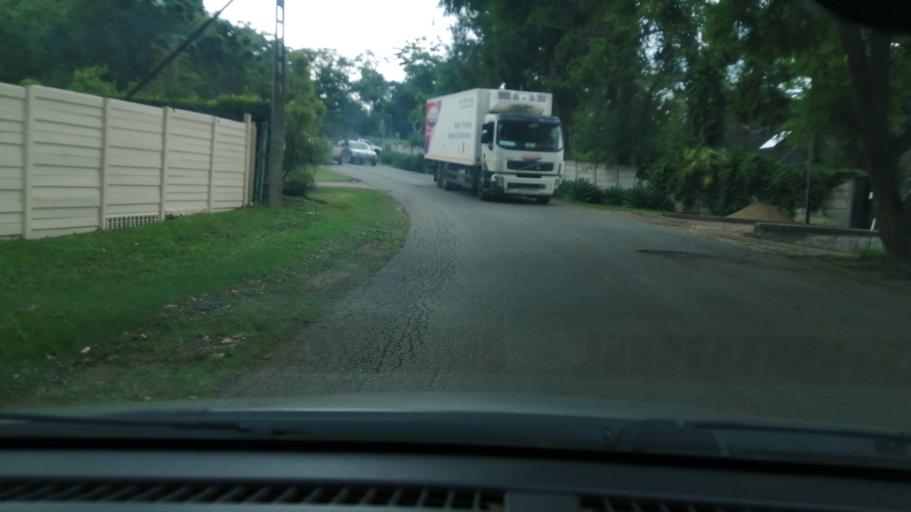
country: ZW
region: Harare
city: Harare
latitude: -17.7724
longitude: 31.0979
